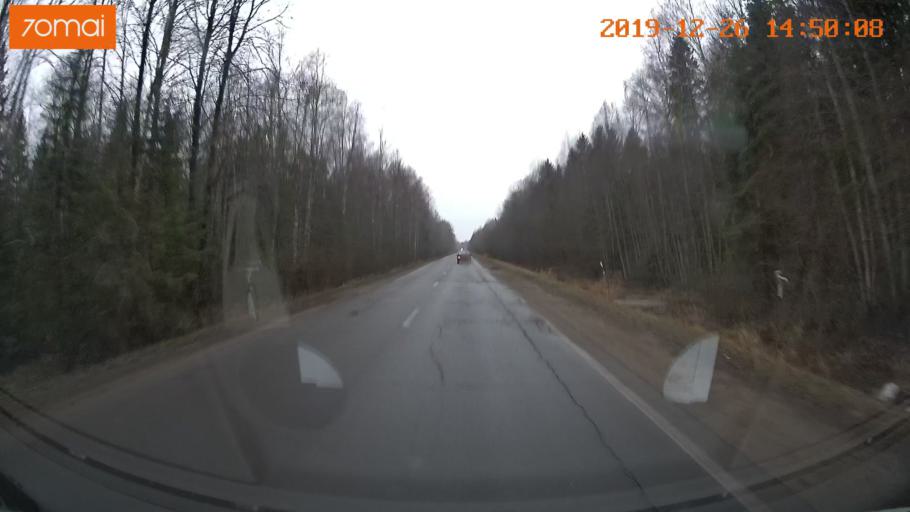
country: RU
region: Jaroslavl
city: Poshekhon'ye
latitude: 58.3344
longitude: 38.9312
